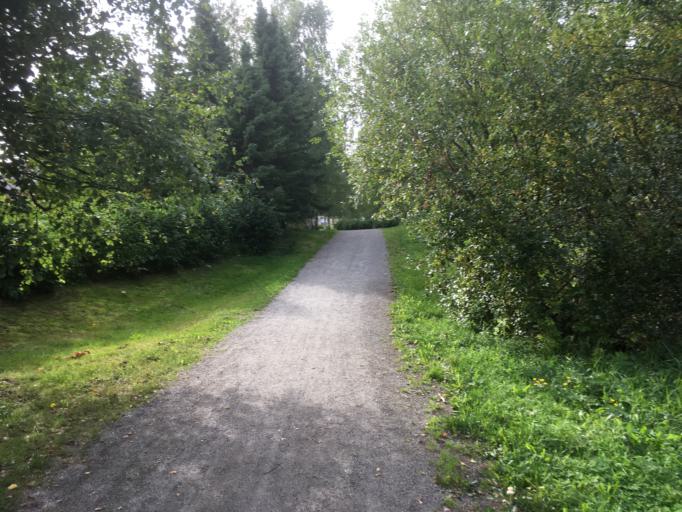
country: FI
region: Central Finland
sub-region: Jyvaeskylae
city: Jyvaeskylae
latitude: 62.2240
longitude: 25.7928
